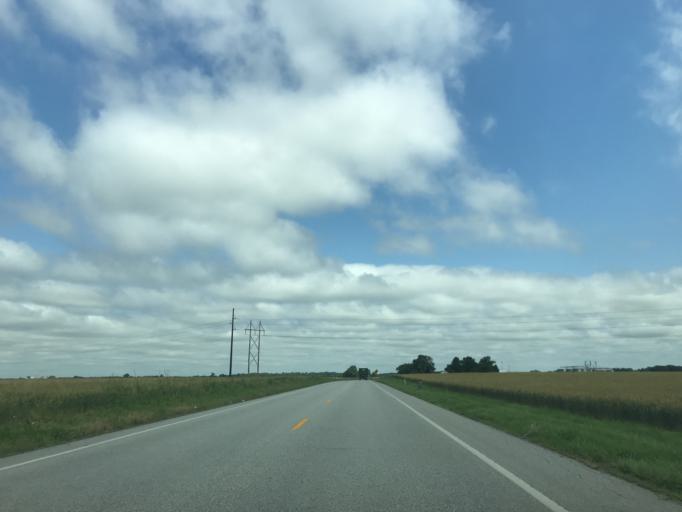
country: US
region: Maryland
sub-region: Caroline County
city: Ridgely
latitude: 38.9240
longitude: -75.8932
